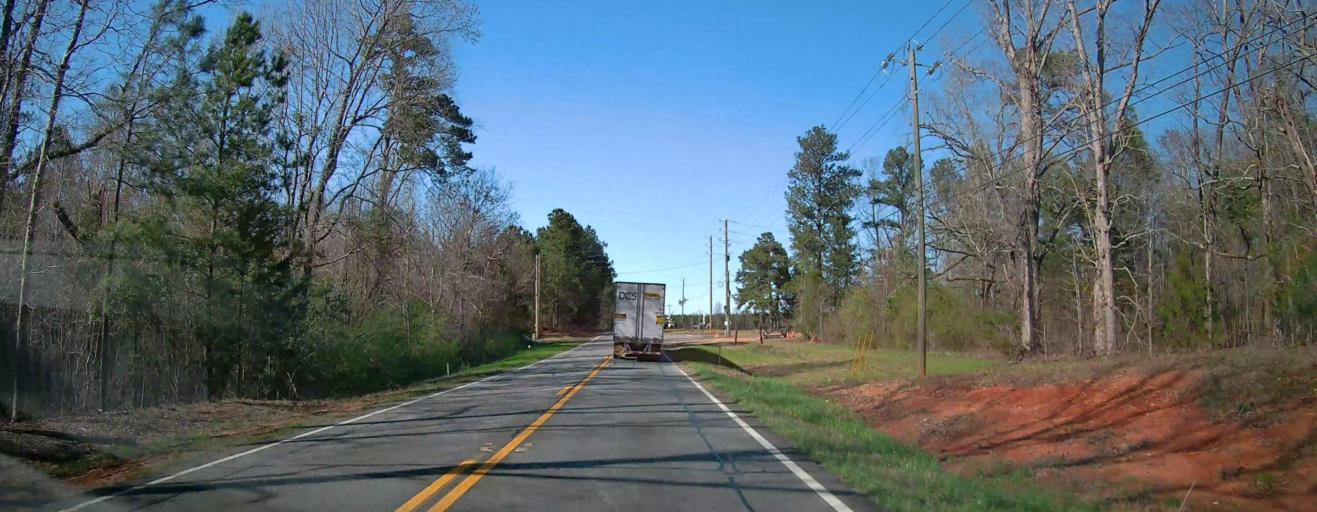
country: US
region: Georgia
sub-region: Butts County
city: Indian Springs
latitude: 33.1600
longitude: -83.9567
